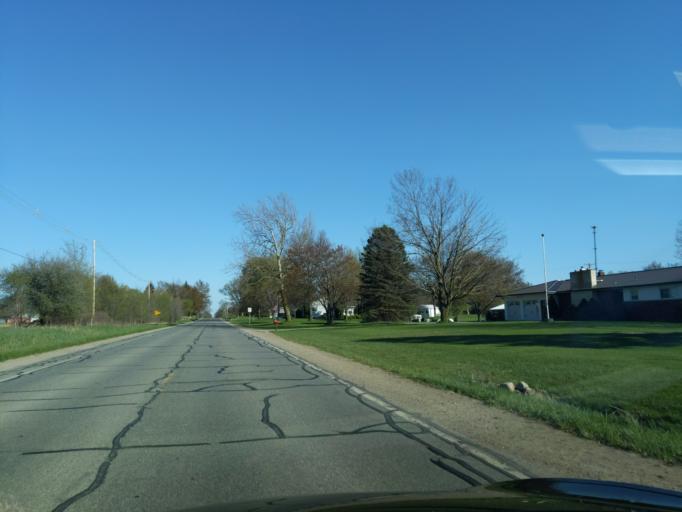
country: US
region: Michigan
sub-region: Ionia County
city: Portland
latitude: 42.8450
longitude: -84.8698
